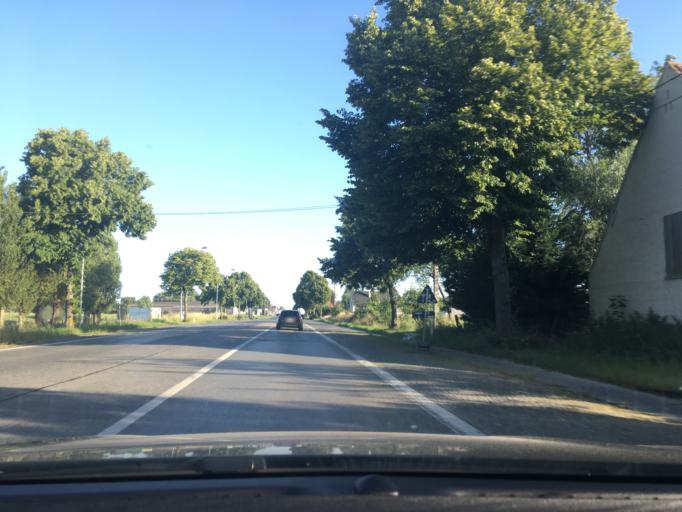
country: BE
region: Flanders
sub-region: Provincie West-Vlaanderen
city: Torhout
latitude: 51.0409
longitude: 3.1073
